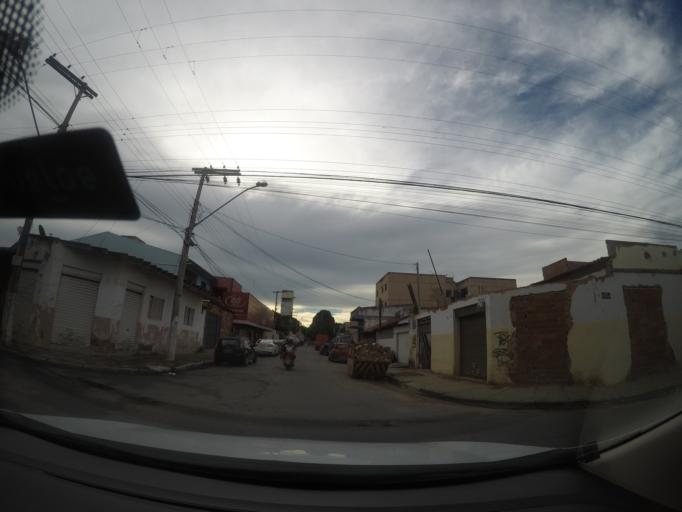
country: BR
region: Goias
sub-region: Goiania
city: Goiania
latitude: -16.6664
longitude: -49.2912
